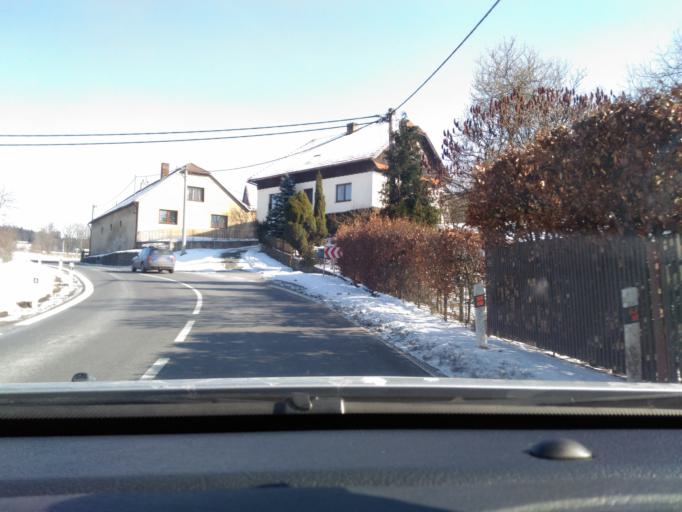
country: CZ
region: Vysocina
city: Bystrice nad Pernstejnem
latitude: 49.5465
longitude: 16.1689
